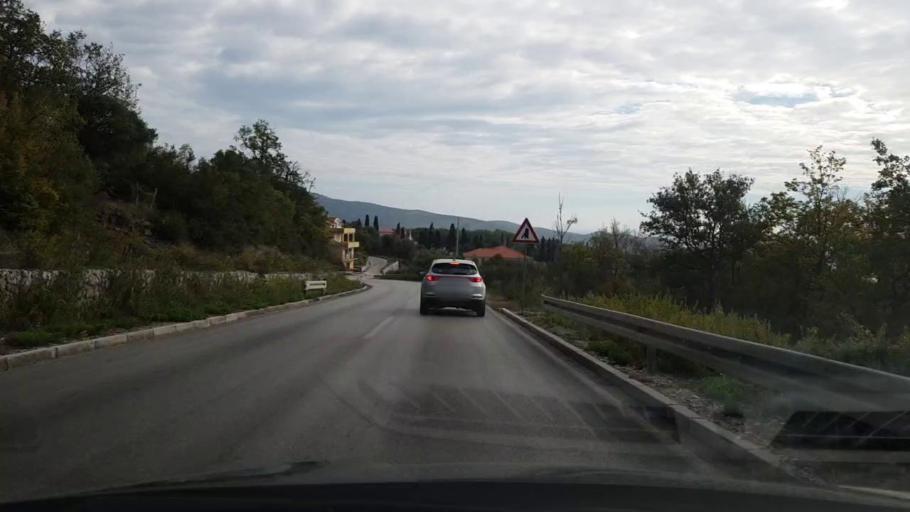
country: ME
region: Herceg Novi
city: Herceg-Novi
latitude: 42.4654
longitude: 18.5448
